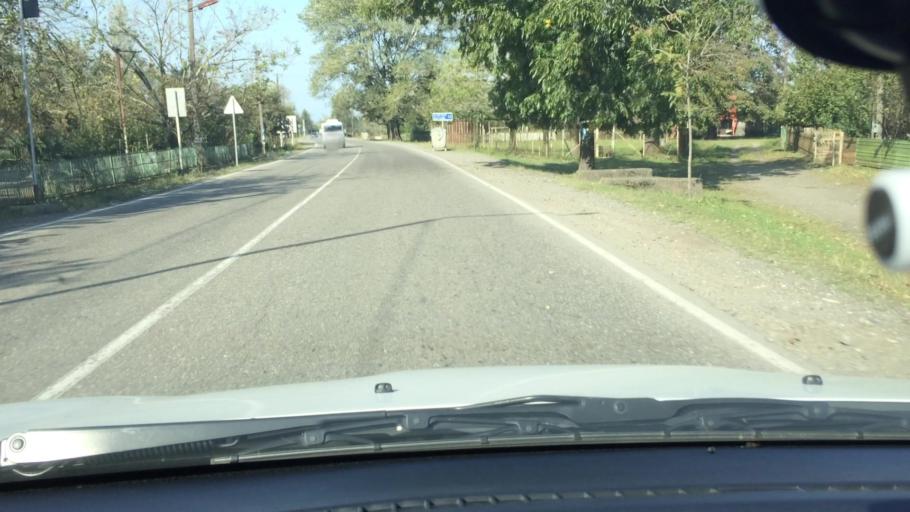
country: GE
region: Guria
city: Lanchkhuti
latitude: 42.0819
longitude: 41.9586
